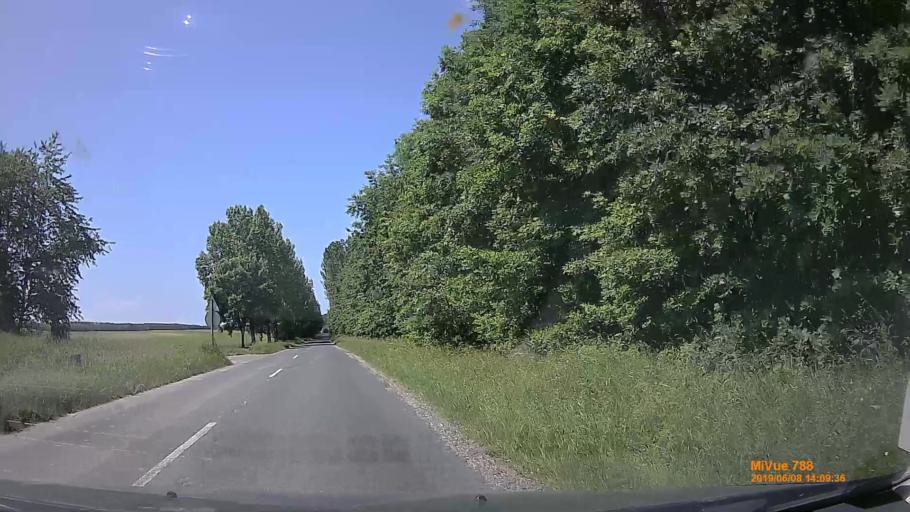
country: HU
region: Vas
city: Buk
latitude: 47.3685
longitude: 16.7361
